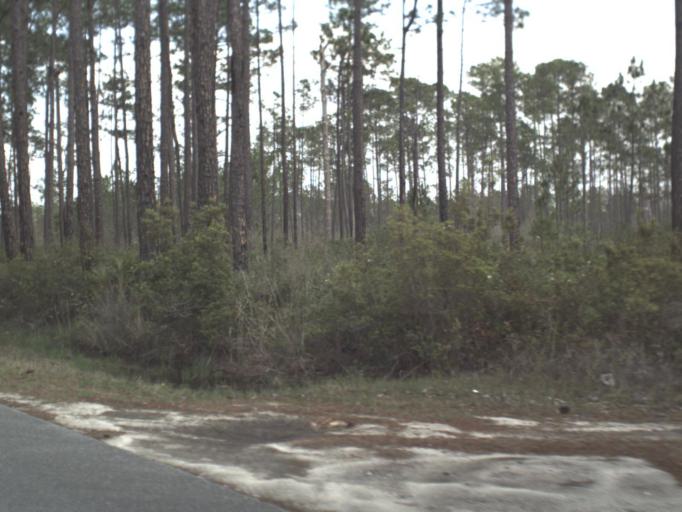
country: US
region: Florida
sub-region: Franklin County
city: Apalachicola
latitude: 29.9629
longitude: -84.9760
